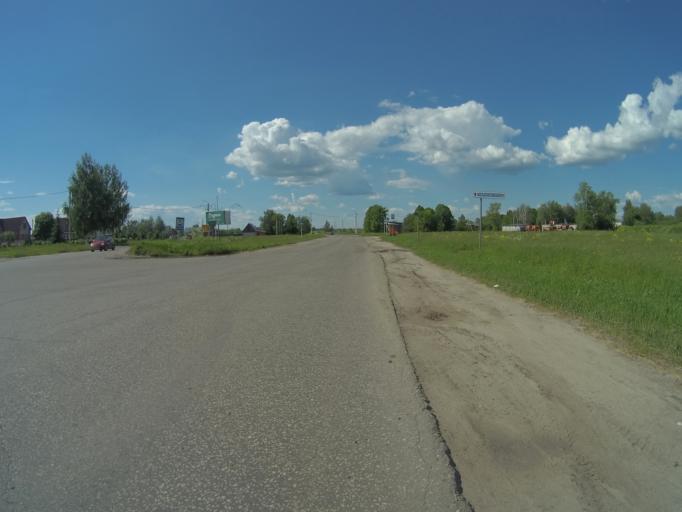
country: RU
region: Vladimir
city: Suzdal'
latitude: 56.4368
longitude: 40.4402
